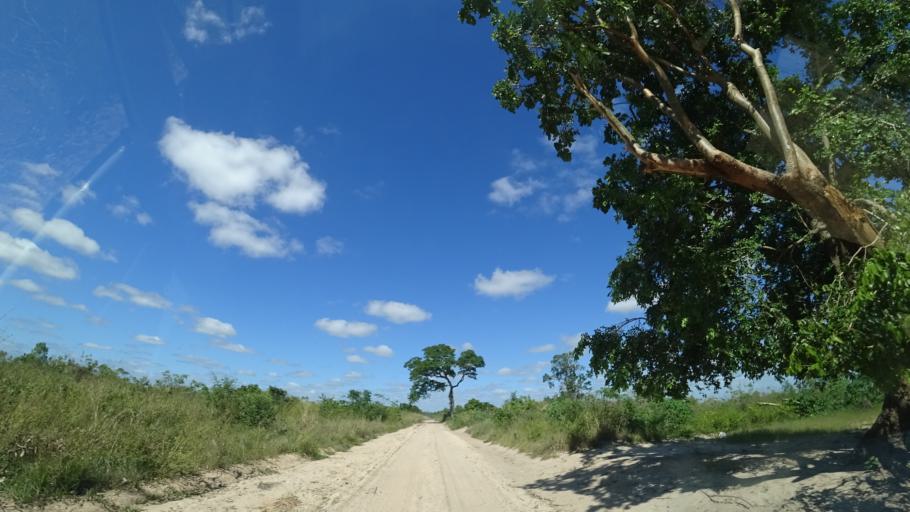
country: MZ
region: Sofala
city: Dondo
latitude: -19.2907
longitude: 34.6889
